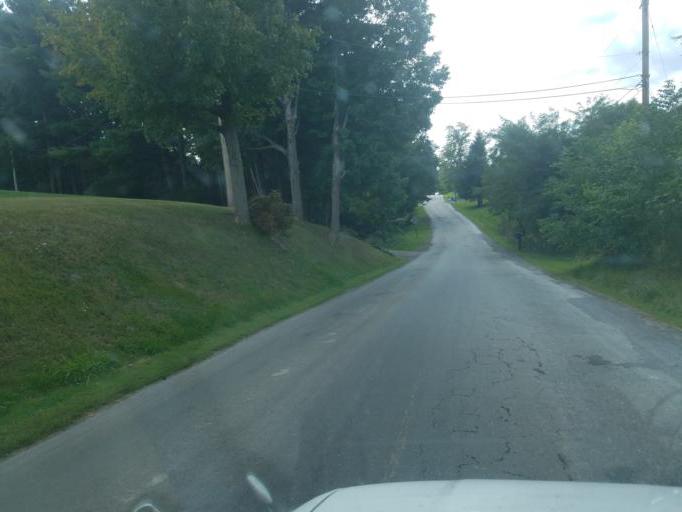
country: US
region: Ohio
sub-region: Geauga County
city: Middlefield
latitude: 41.4571
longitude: -80.9750
